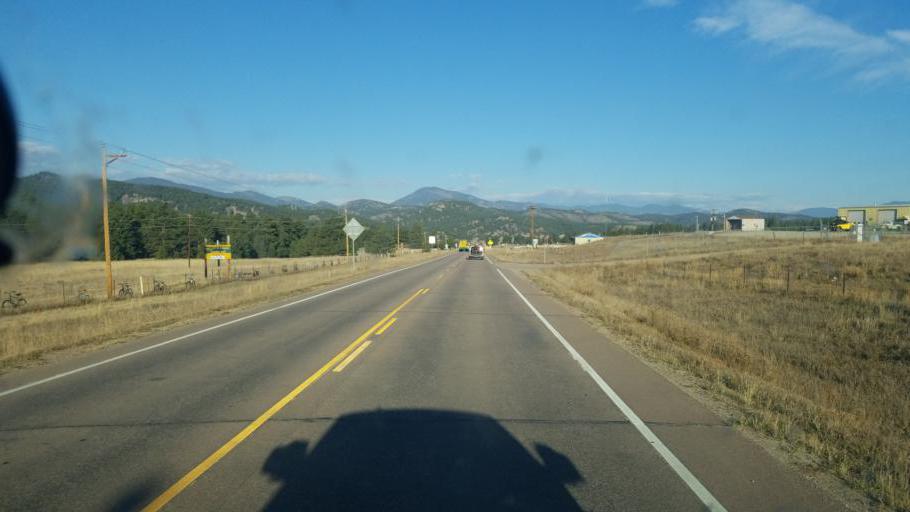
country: US
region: Colorado
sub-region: Teller County
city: Cripple Creek
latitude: 38.9713
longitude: -105.3453
